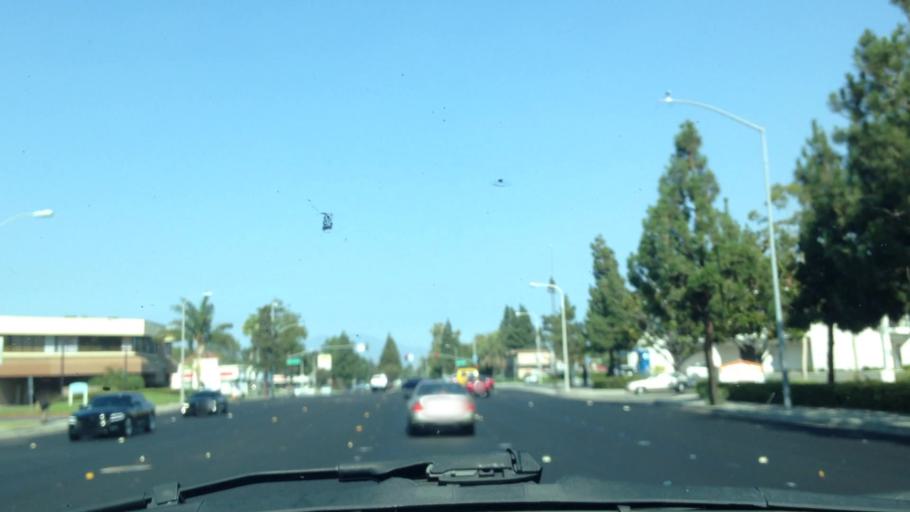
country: US
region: California
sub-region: Orange County
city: Santa Ana
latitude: 33.7000
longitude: -117.8874
